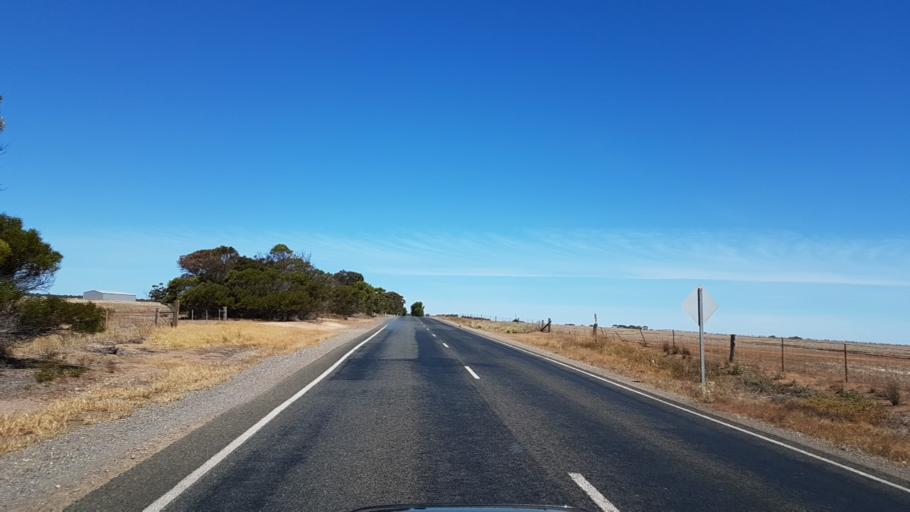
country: AU
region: South Australia
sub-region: Yorke Peninsula
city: Maitland
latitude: -34.3450
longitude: 137.6598
